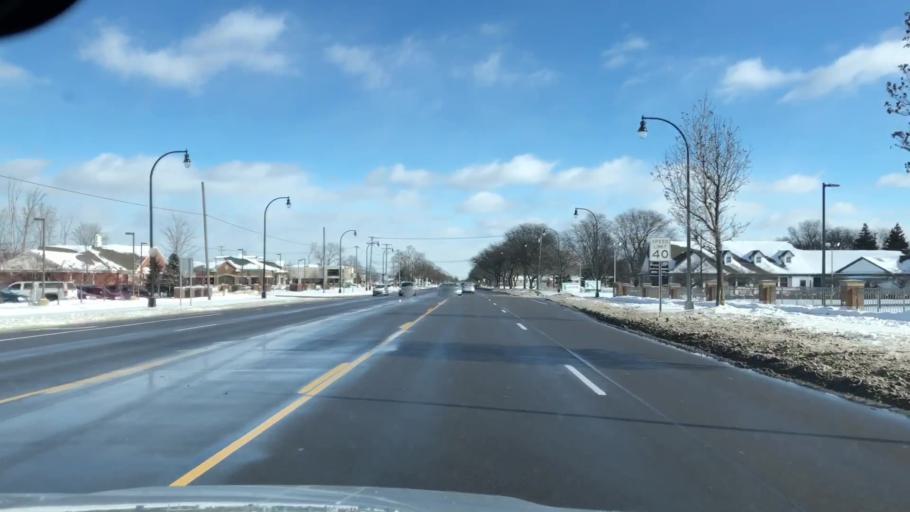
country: US
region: Michigan
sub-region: Wayne County
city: Livonia
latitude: 42.3683
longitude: -83.3708
